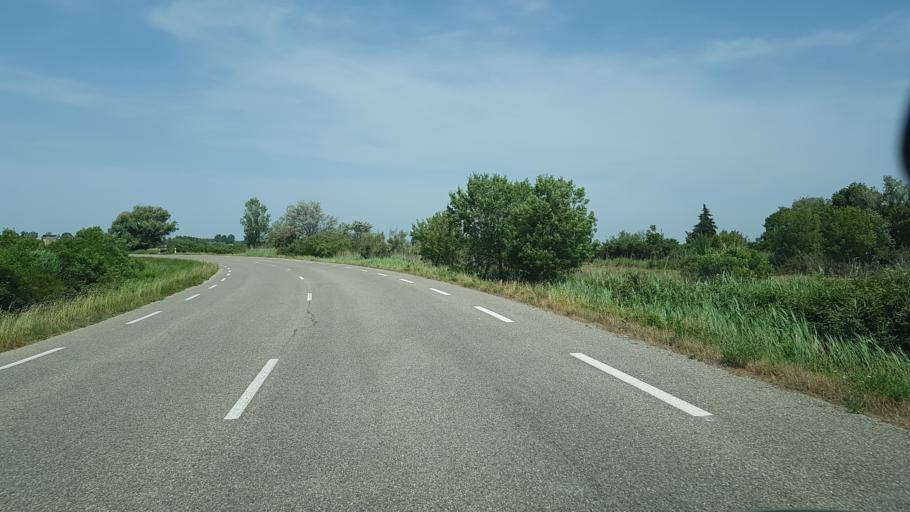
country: FR
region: Languedoc-Roussillon
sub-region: Departement du Gard
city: Saint-Gilles
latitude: 43.6044
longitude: 4.4887
